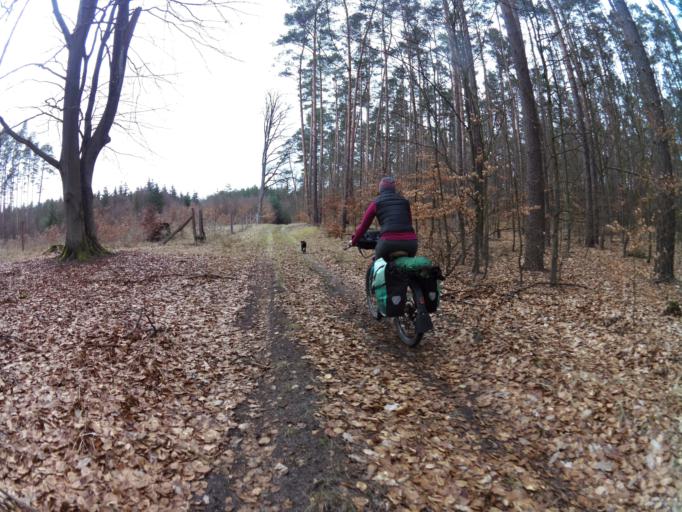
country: PL
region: Lubusz
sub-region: Powiat gorzowski
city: Witnica
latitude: 52.7674
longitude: 14.8299
